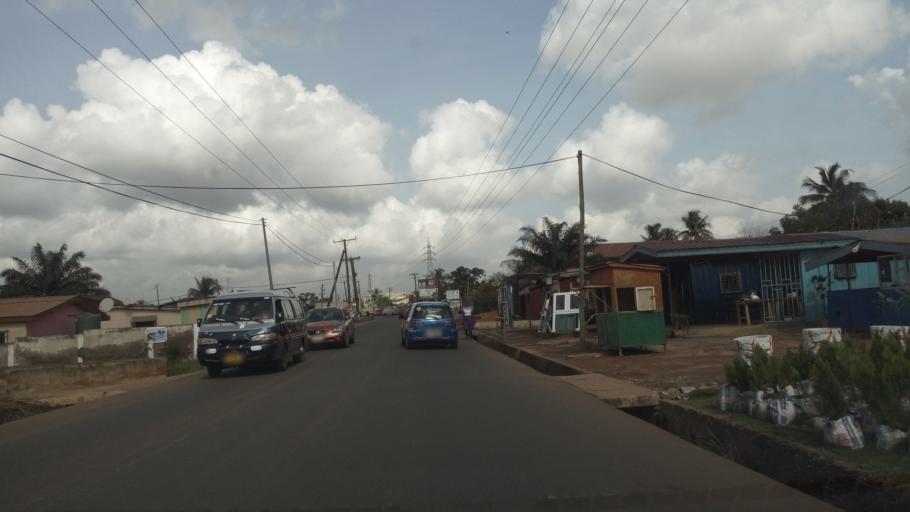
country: GH
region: Greater Accra
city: Medina Estates
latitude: 5.6599
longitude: -0.1542
